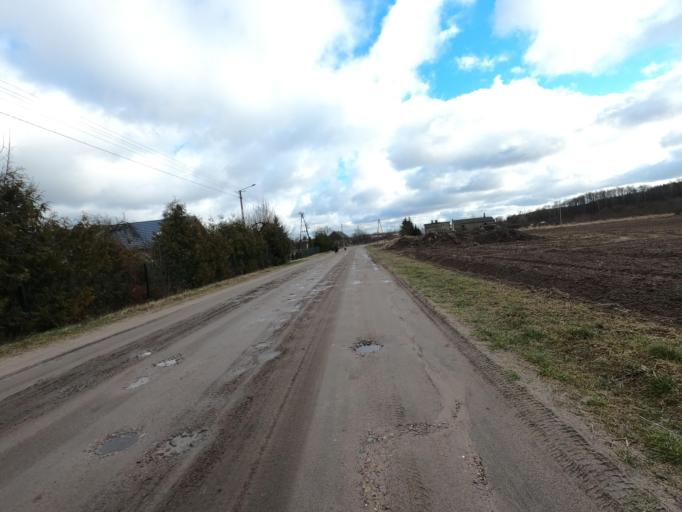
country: PL
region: Greater Poland Voivodeship
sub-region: Powiat pilski
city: Miasteczko Krajenskie
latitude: 53.1141
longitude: 16.9941
